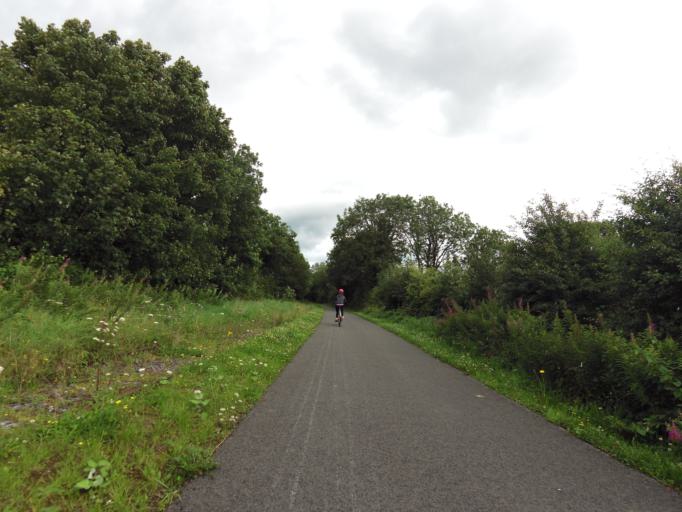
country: IE
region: Leinster
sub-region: An Iarmhi
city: An Muileann gCearr
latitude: 53.5108
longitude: -7.3802
